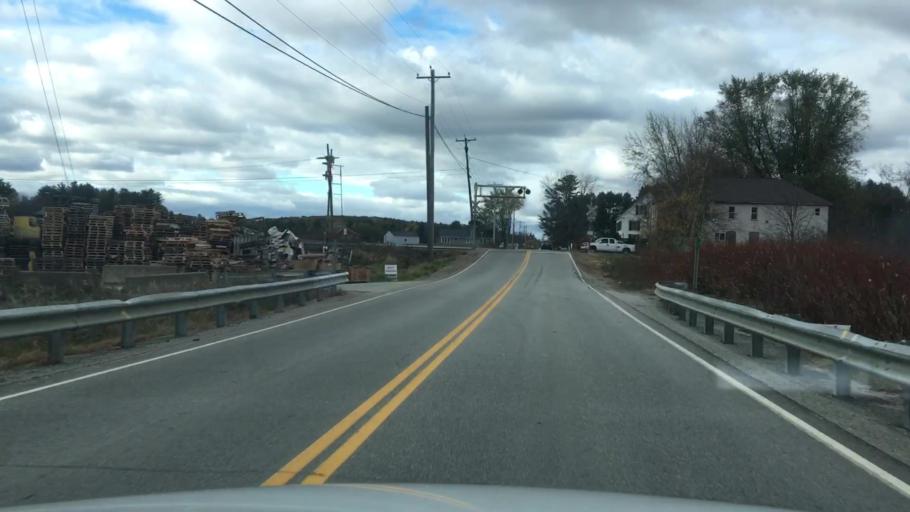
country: US
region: Maine
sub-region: Kennebec County
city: Monmouth
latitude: 44.2059
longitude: -70.0788
